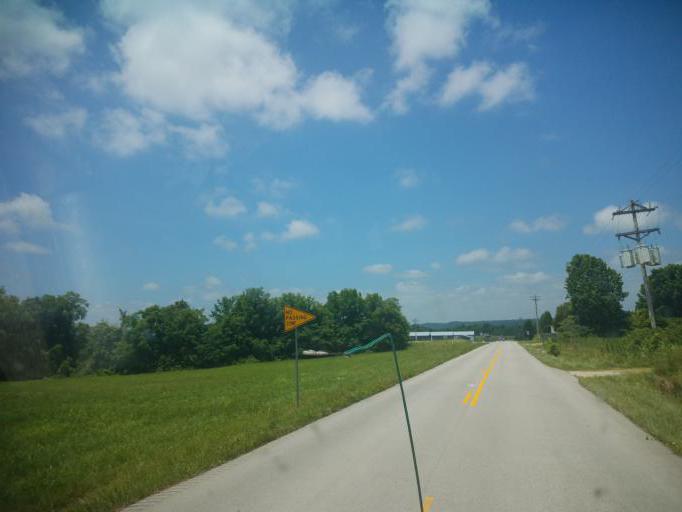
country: US
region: Kentucky
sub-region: Edmonson County
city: Brownsville
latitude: 37.3240
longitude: -86.1185
